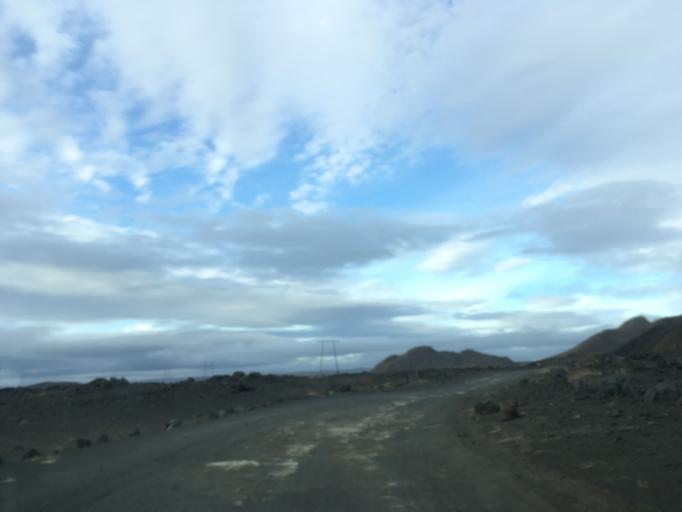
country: IS
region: South
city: Vestmannaeyjar
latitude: 64.1008
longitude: -19.1069
